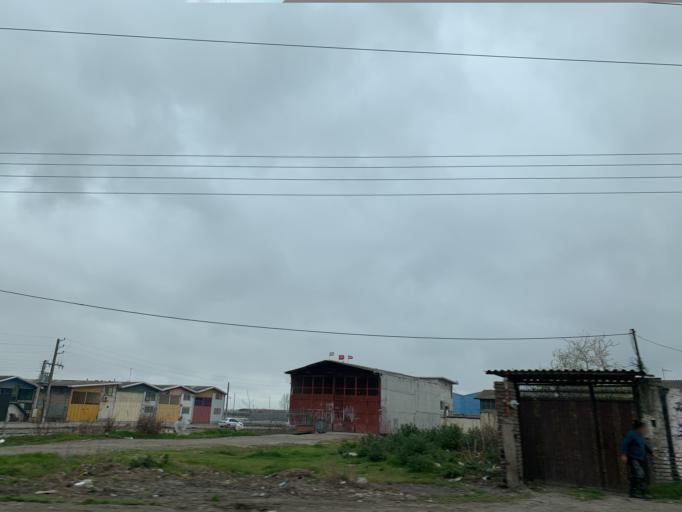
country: IR
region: Mazandaran
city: Babol
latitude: 36.5304
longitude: 52.6350
